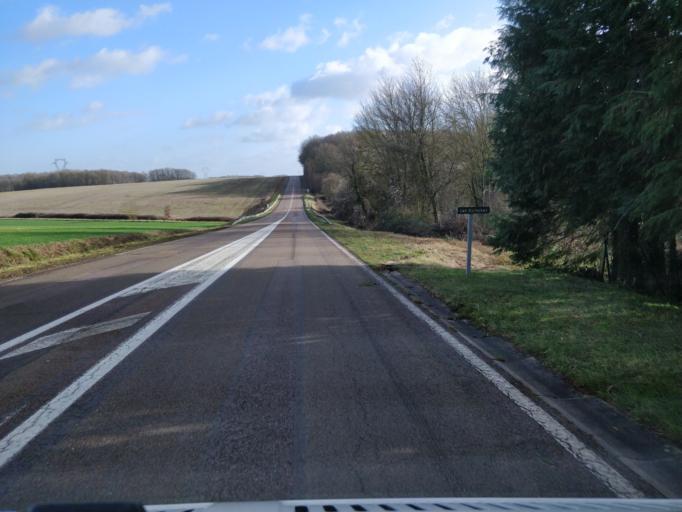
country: FR
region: Bourgogne
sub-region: Departement de l'Yonne
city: Cheroy
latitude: 48.1988
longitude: 3.0170
